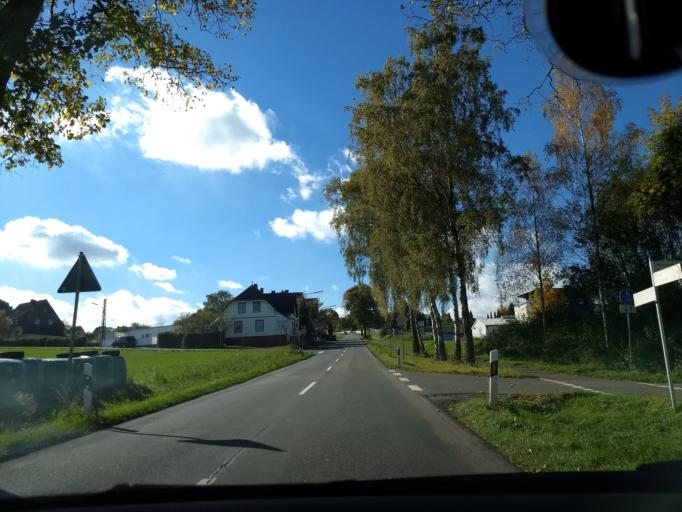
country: DE
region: North Rhine-Westphalia
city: Warstein
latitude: 51.4615
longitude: 8.3847
